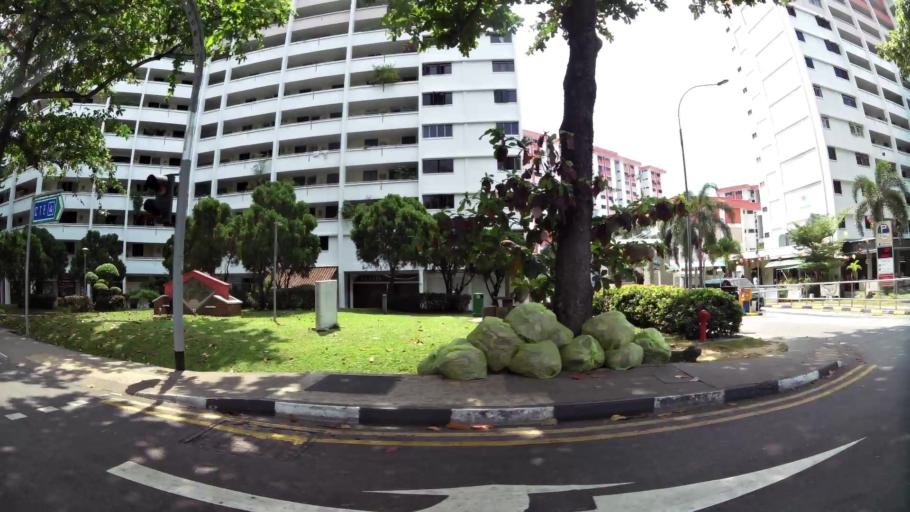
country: SG
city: Singapore
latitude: 1.2777
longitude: 103.8316
